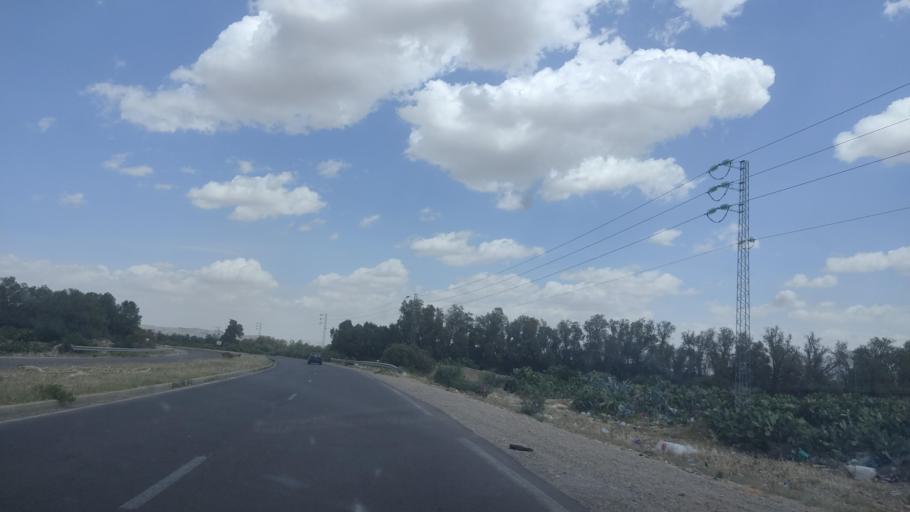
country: TN
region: Al Qasrayn
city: Kasserine
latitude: 35.1976
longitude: 8.8677
